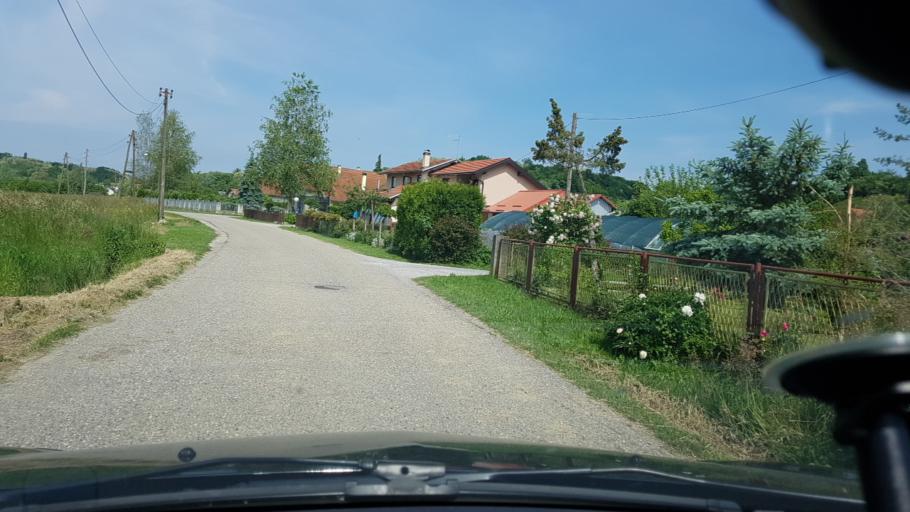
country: HR
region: Krapinsko-Zagorska
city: Selnica
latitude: 46.0192
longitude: 16.0628
